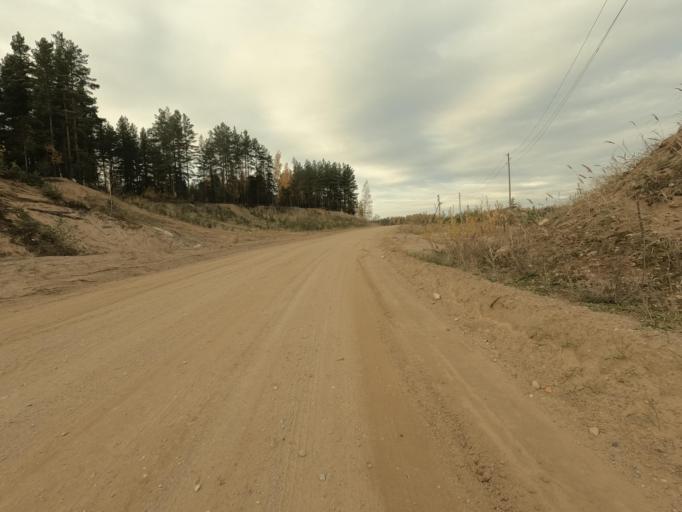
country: RU
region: Leningrad
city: Priladozhskiy
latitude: 59.7080
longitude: 31.3637
